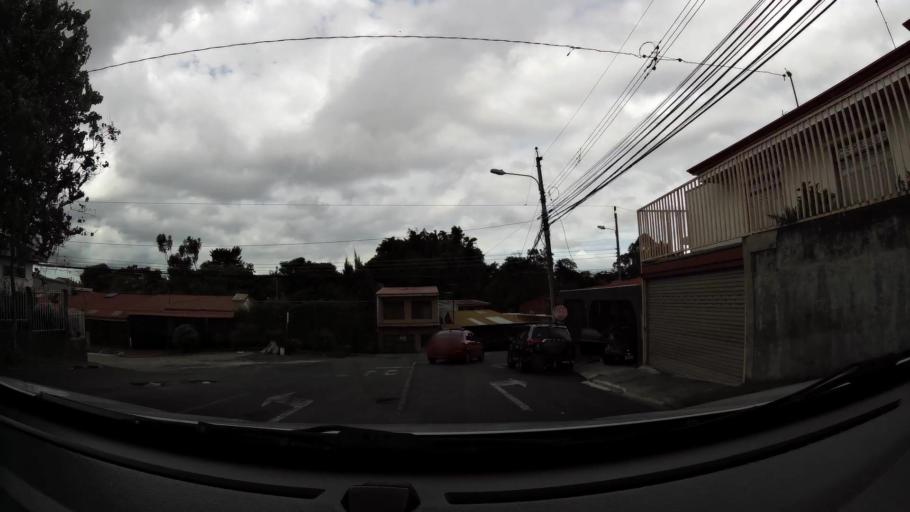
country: CR
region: San Jose
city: San Pedro
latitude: 9.9232
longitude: -84.0513
